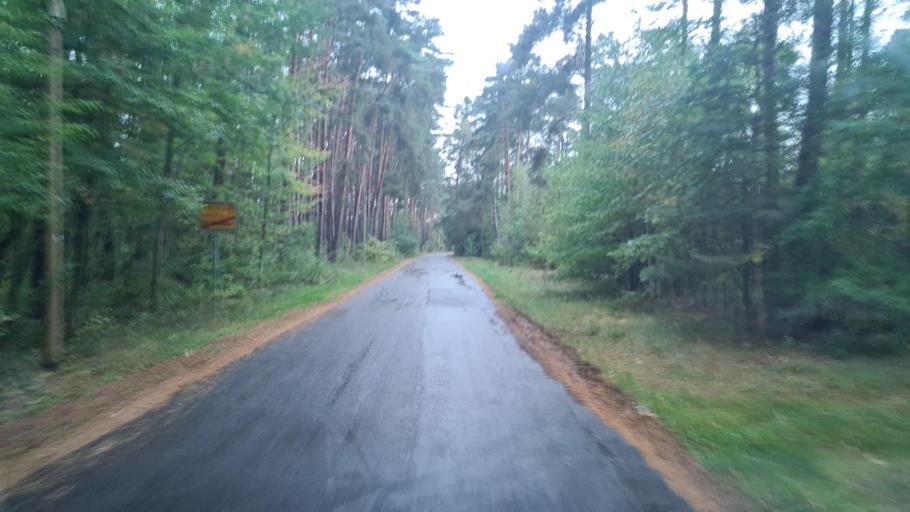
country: DE
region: Brandenburg
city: Munchehofe
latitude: 52.1305
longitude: 13.9423
